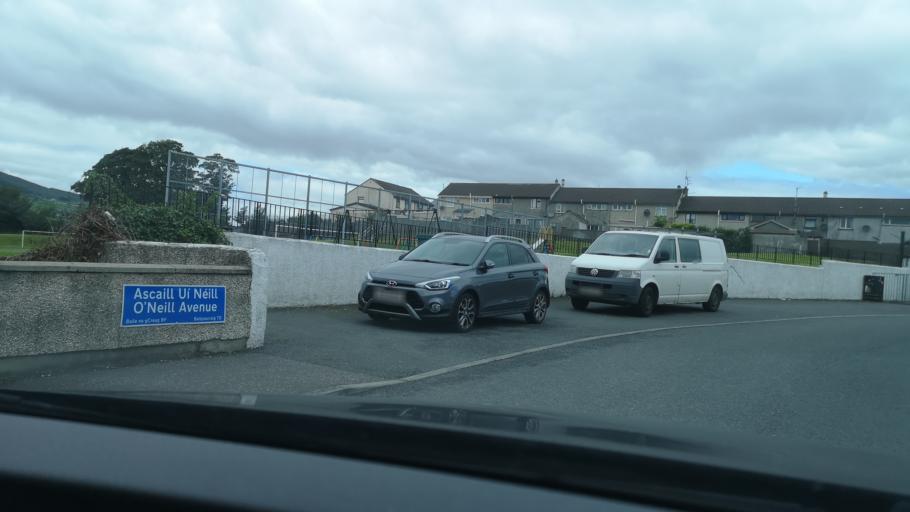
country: GB
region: Northern Ireland
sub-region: Newry and Mourne District
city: Newry
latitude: 54.1681
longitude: -6.3290
